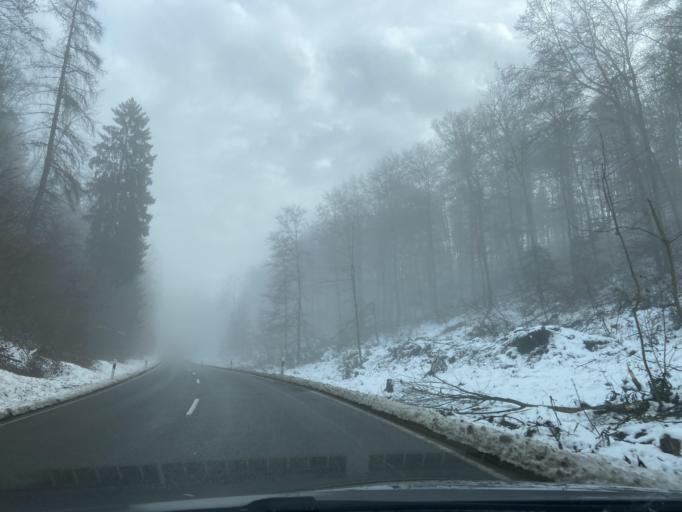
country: DE
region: Baden-Wuerttemberg
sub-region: Tuebingen Region
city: Veringenstadt
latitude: 48.1774
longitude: 9.2392
